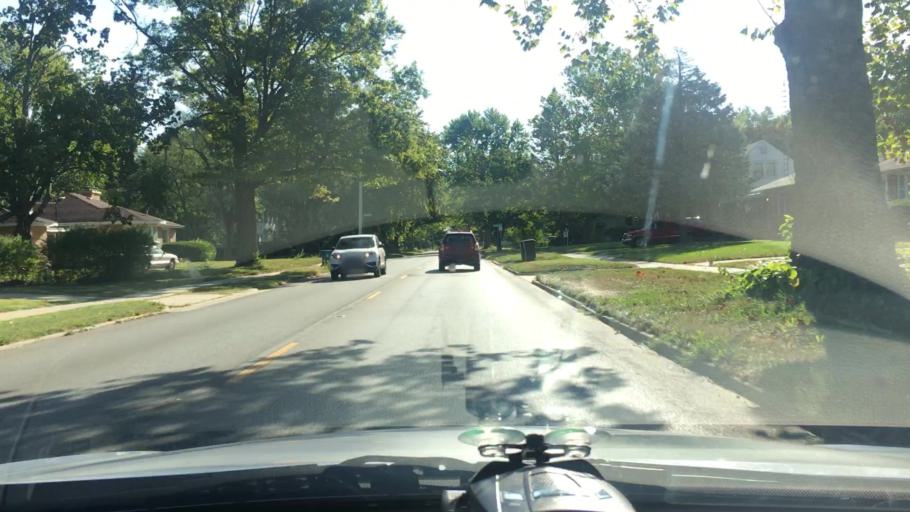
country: US
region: Illinois
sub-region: Champaign County
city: Champaign
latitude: 40.1127
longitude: -88.2636
